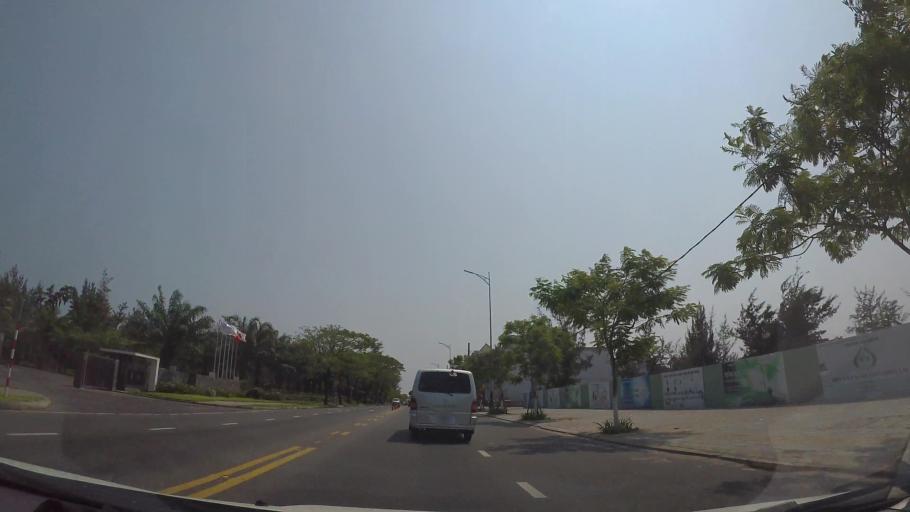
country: VN
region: Da Nang
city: Ngu Hanh Son
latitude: 16.0001
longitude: 108.2674
